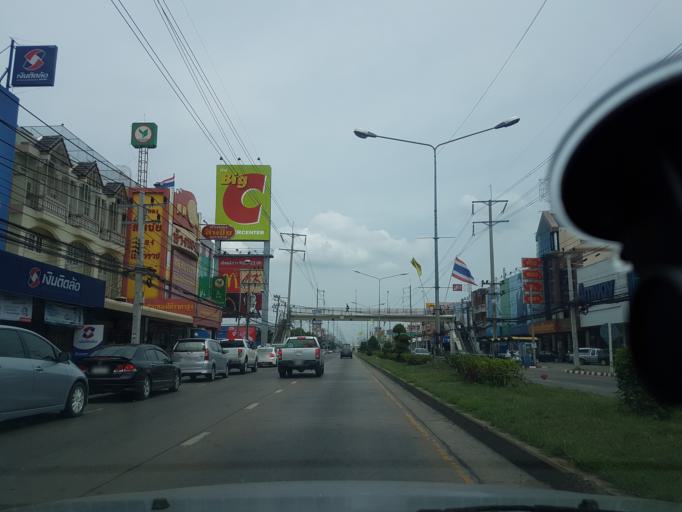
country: TH
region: Lop Buri
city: Lop Buri
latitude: 14.7929
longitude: 100.6704
